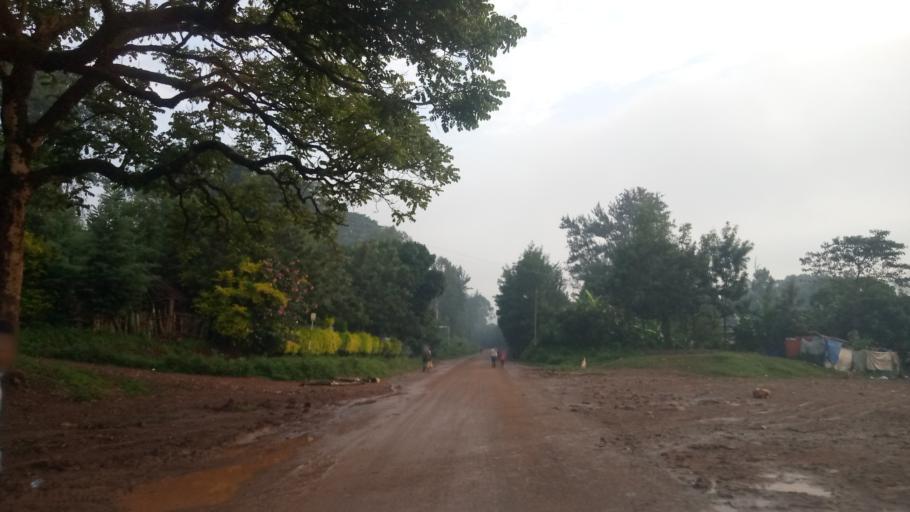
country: ET
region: Oromiya
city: Jima
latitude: 7.6823
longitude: 36.8337
